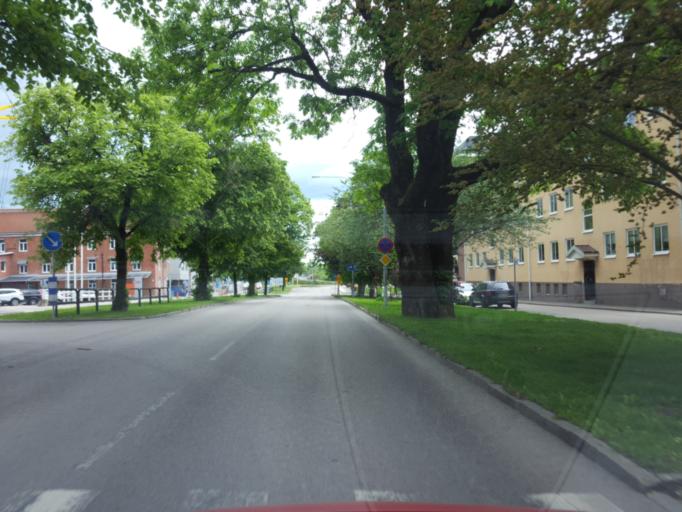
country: SE
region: Vaestra Goetaland
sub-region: Trollhattan
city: Trollhattan
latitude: 58.2865
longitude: 12.2955
